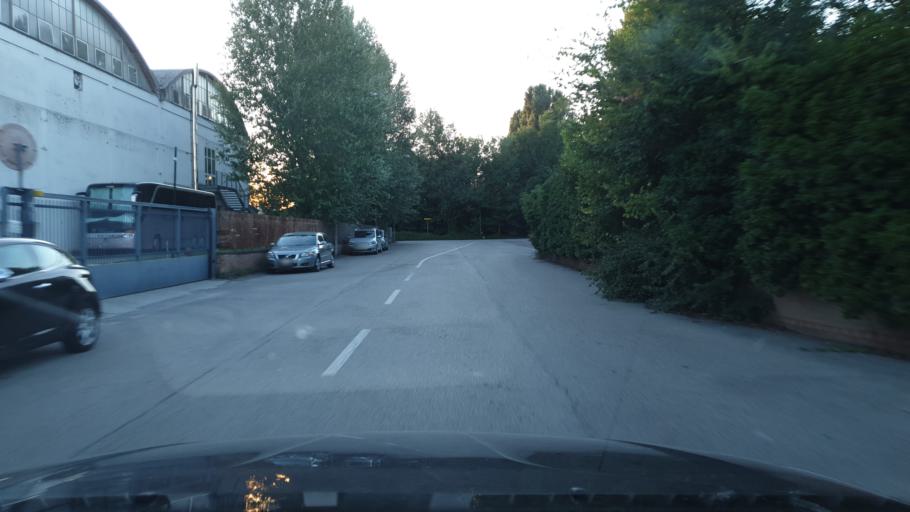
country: IT
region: Emilia-Romagna
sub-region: Provincia di Bologna
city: Progresso
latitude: 44.5520
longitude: 11.3917
